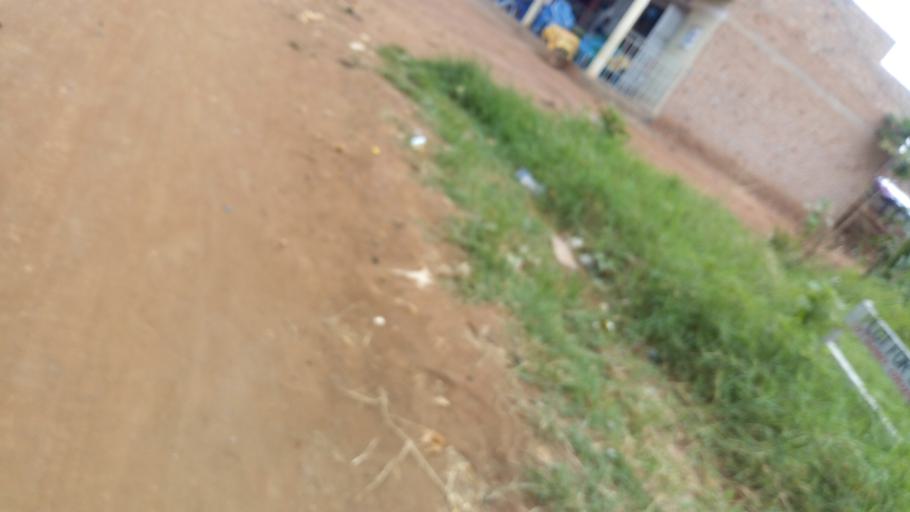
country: UG
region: Western Region
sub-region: Kiryandongo District
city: Kiryandongo
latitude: 1.8075
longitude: 32.0114
